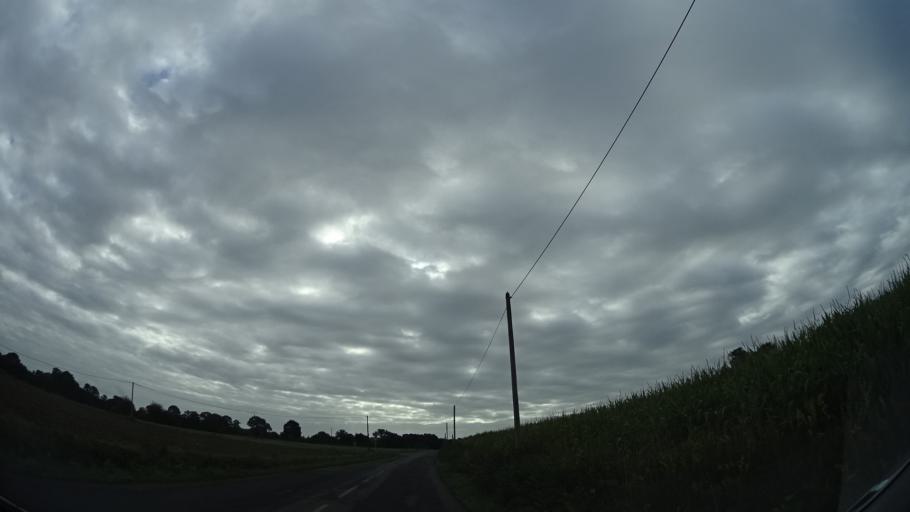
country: FR
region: Brittany
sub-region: Departement d'Ille-et-Vilaine
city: Montreuil-sur-Ille
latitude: 48.3388
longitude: -1.6565
